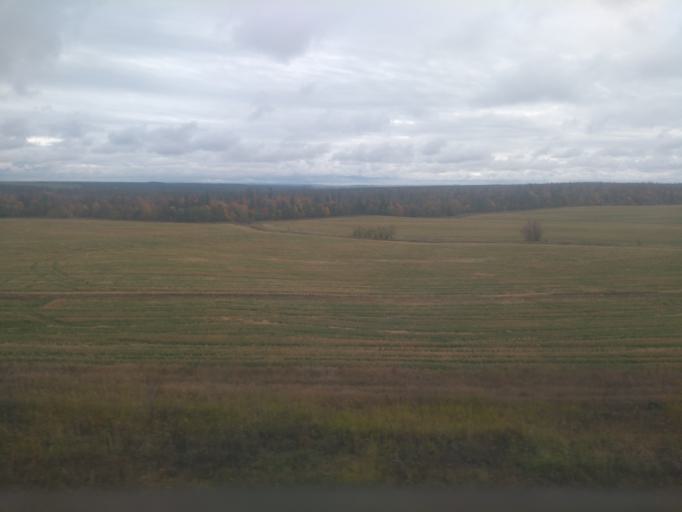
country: RU
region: Udmurtiya
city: Alnashi
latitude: 56.1530
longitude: 52.5798
